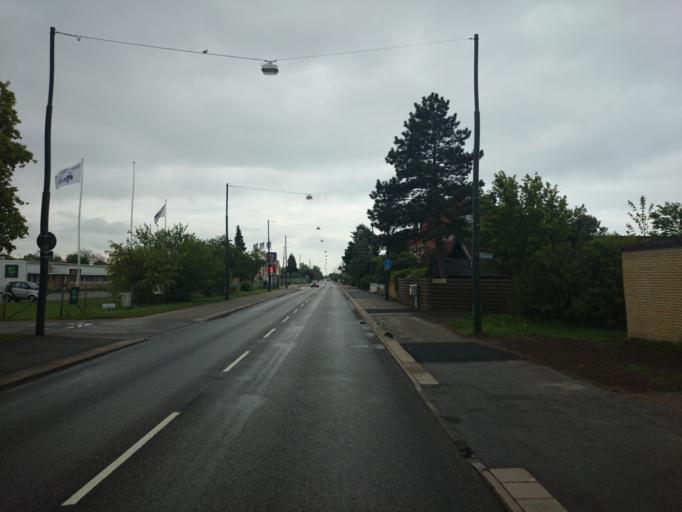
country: SE
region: Skane
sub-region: Malmo
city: Bunkeflostrand
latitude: 55.5617
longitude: 12.9195
